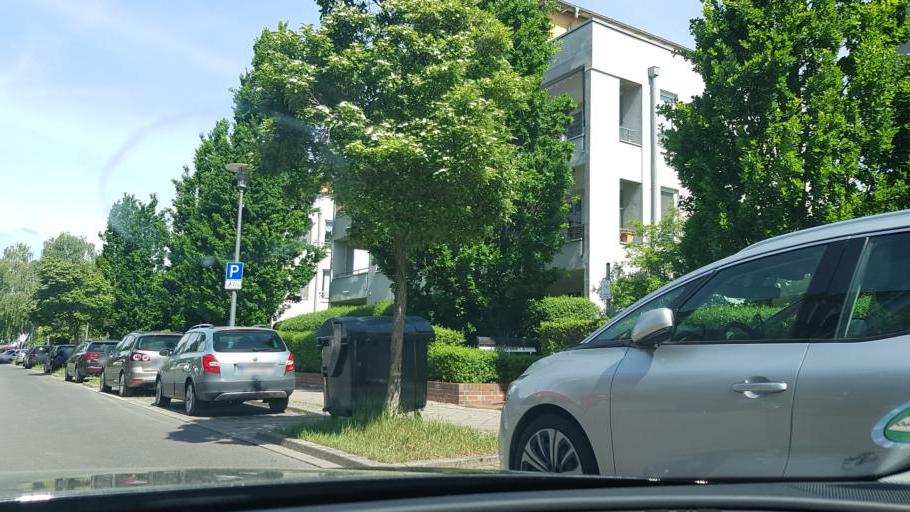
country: DE
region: Berlin
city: Buchholz
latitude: 52.6055
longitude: 13.4264
